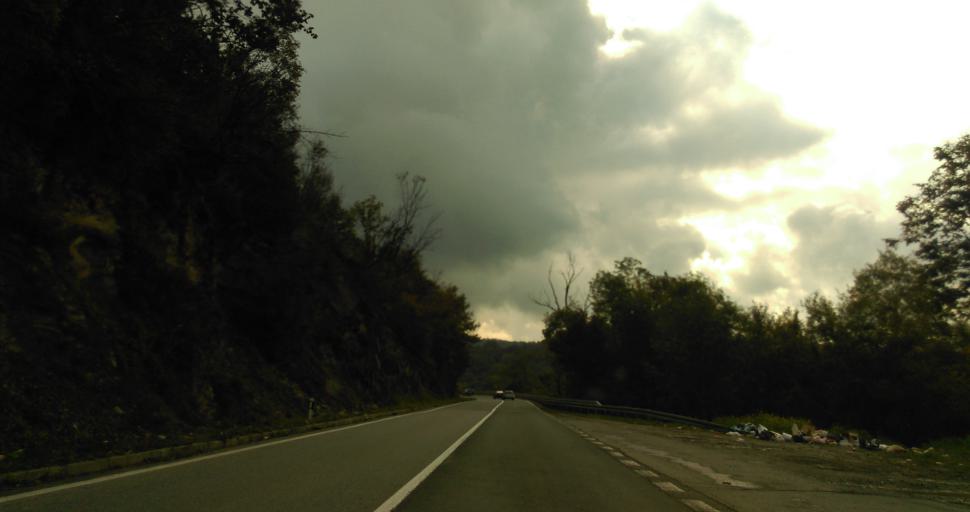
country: RS
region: Central Serbia
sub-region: Kolubarski Okrug
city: Ljig
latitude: 44.1896
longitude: 20.3218
